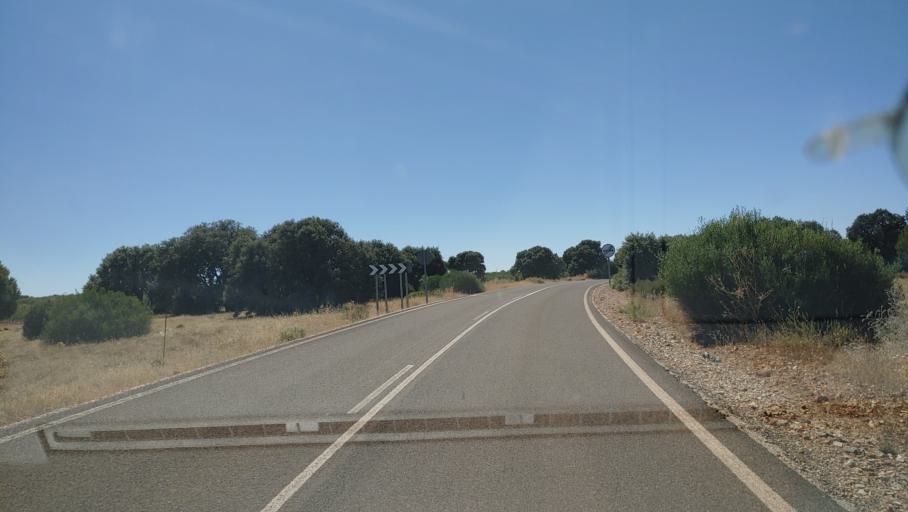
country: ES
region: Castille-La Mancha
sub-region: Provincia de Ciudad Real
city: Villahermosa
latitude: 38.8352
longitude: -2.8201
